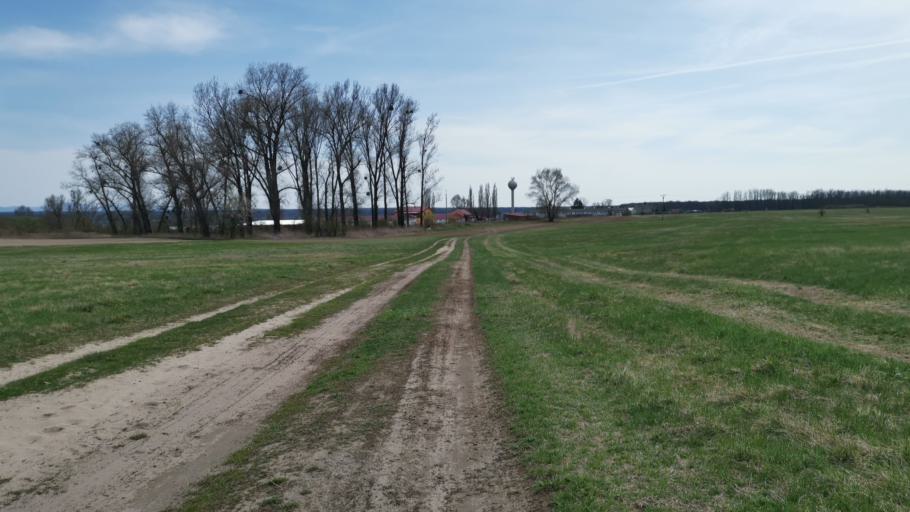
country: SK
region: Trnavsky
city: Gbely
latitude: 48.6629
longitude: 17.0995
